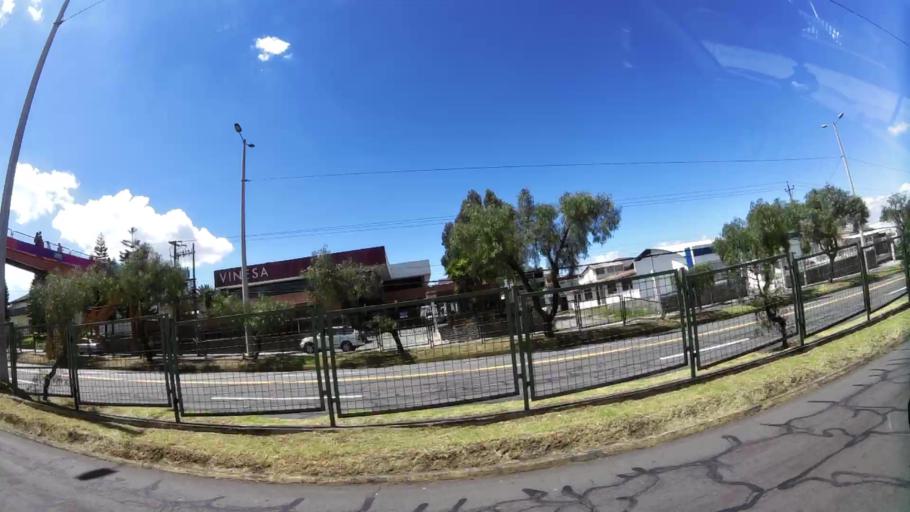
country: EC
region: Pichincha
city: Quito
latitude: -0.1318
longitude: -78.4817
